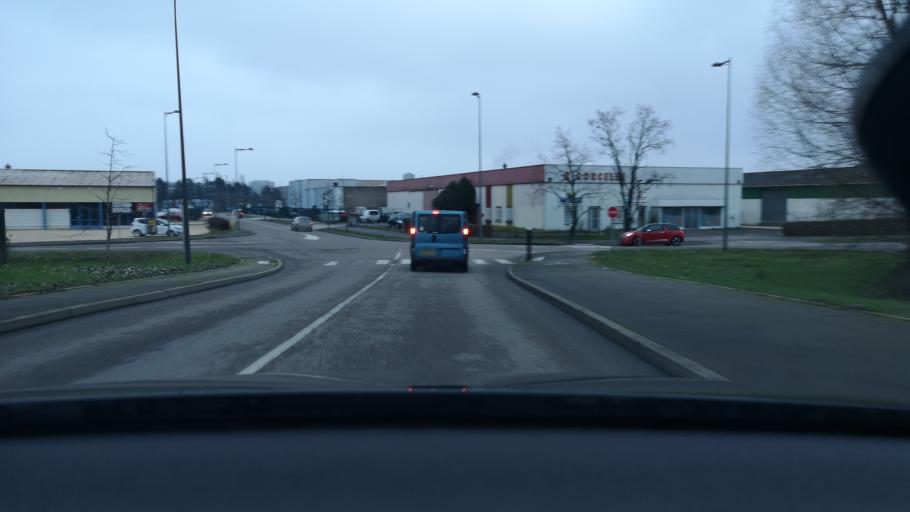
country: FR
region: Bourgogne
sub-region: Departement de Saone-et-Loire
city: Chatenoy-le-Royal
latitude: 46.7980
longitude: 4.8280
